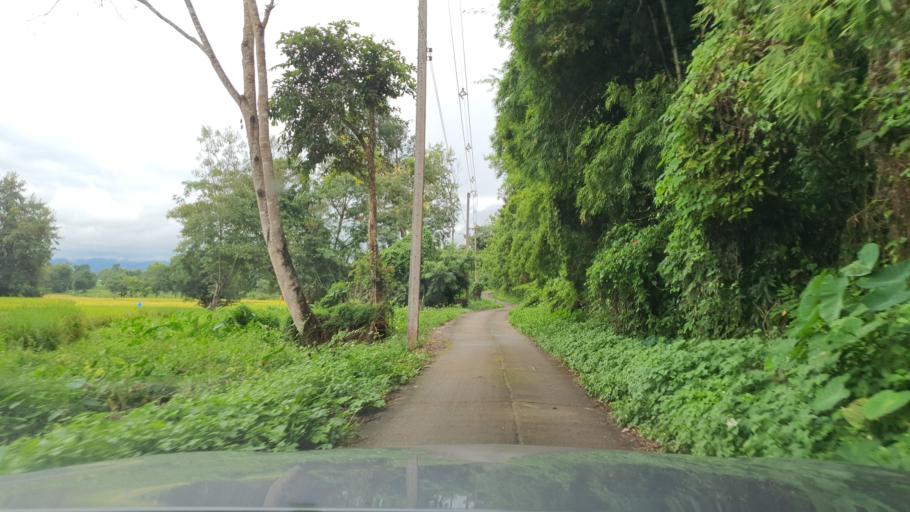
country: TH
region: Chiang Mai
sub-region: Amphoe Chiang Dao
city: Chiang Dao
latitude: 19.3373
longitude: 98.9270
